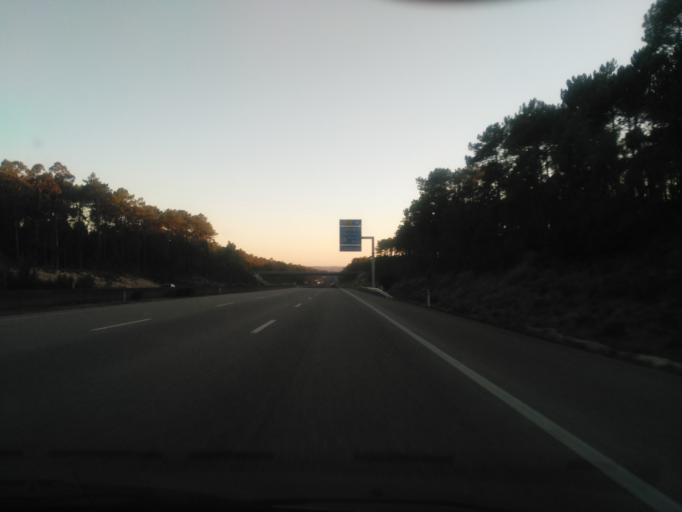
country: PT
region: Leiria
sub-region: Alcobaca
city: Pataias
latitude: 39.6587
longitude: -8.9594
